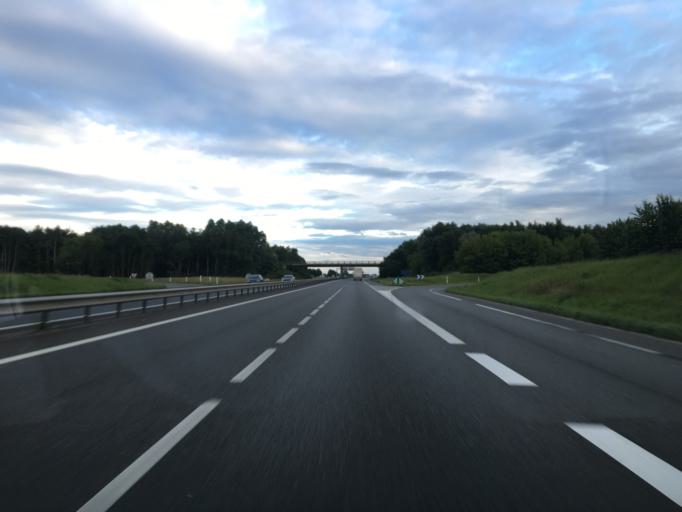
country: FR
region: Ile-de-France
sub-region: Departement de Seine-et-Marne
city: Moissy-Cramayel
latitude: 48.6160
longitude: 2.6312
